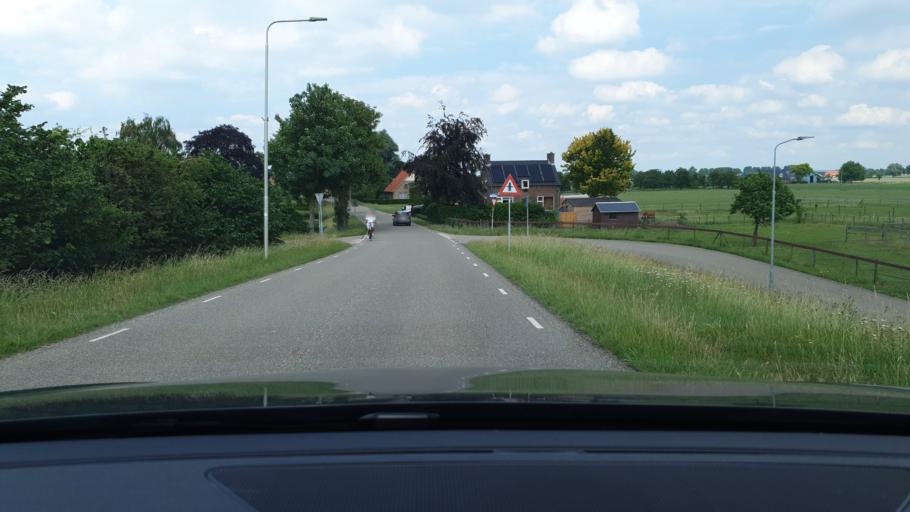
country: NL
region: Gelderland
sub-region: Gemeente Overbetuwe
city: Elst
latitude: 51.9022
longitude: 5.8918
